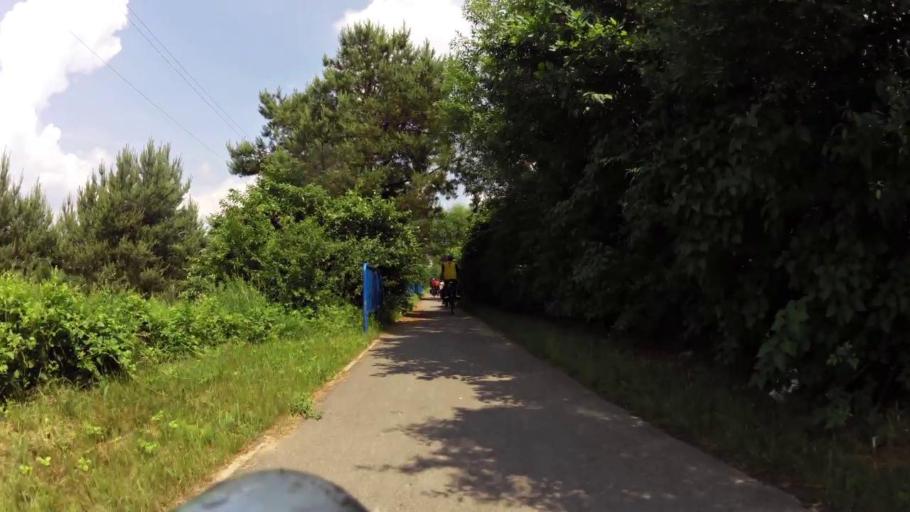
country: PL
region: Kujawsko-Pomorskie
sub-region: Powiat bydgoski
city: Koronowo
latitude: 53.2845
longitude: 17.9405
